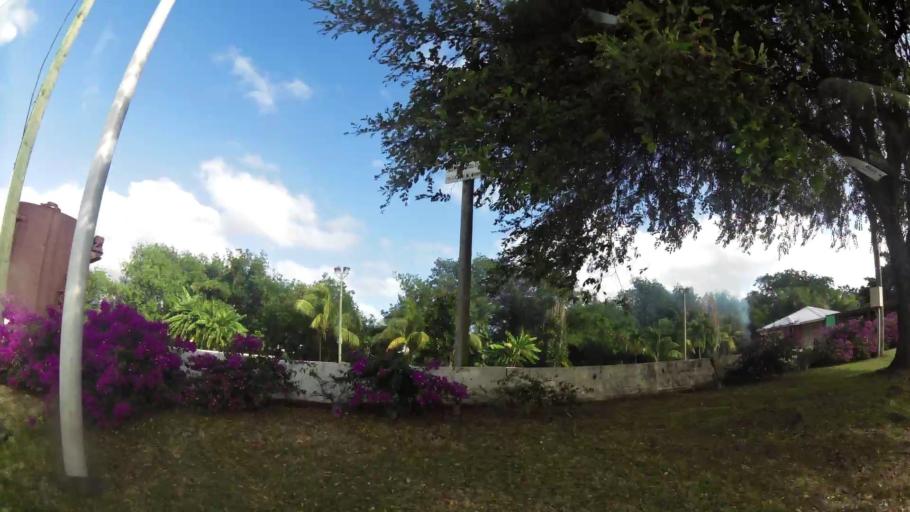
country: MQ
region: Martinique
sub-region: Martinique
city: Le Francois
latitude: 14.6171
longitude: -60.9067
